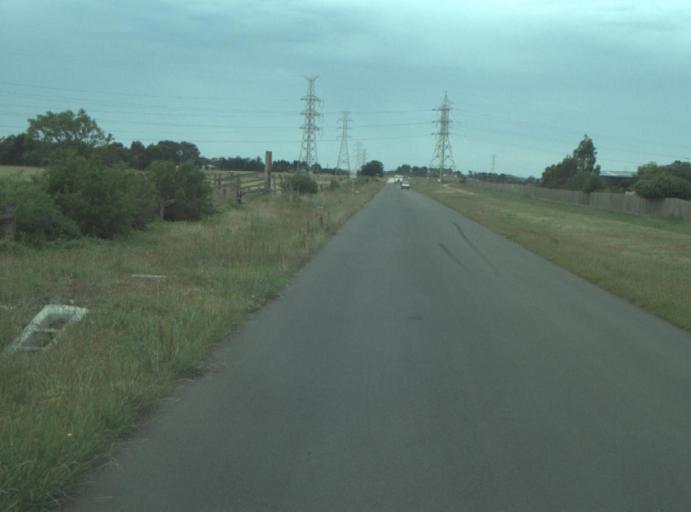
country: AU
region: Victoria
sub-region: Greater Geelong
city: Breakwater
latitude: -38.1937
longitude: 144.3988
